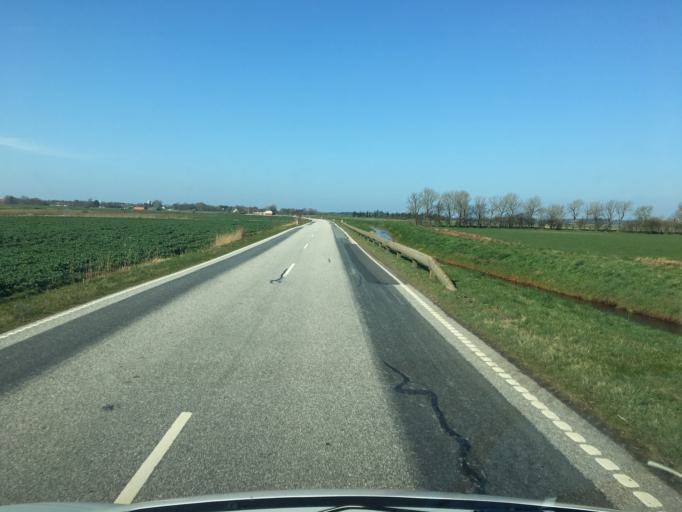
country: DE
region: Schleswig-Holstein
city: Aventoft
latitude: 55.0184
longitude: 8.7489
